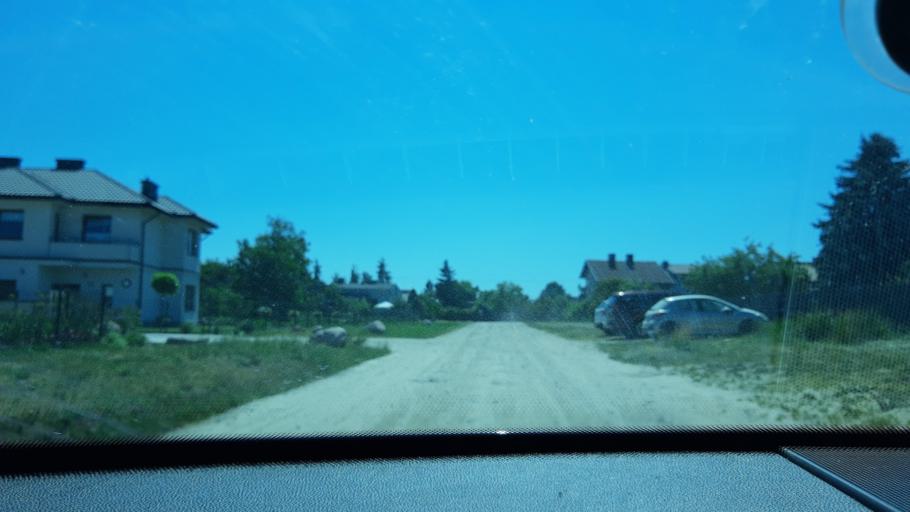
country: PL
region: Lodz Voivodeship
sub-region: Powiat sieradzki
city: Sieradz
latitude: 51.5851
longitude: 18.7340
